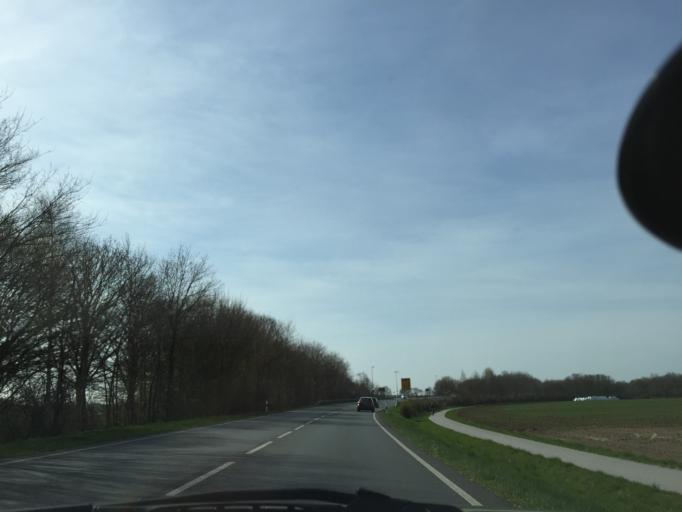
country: DE
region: North Rhine-Westphalia
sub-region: Regierungsbezirk Dusseldorf
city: Goch
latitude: 51.7205
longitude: 6.1584
